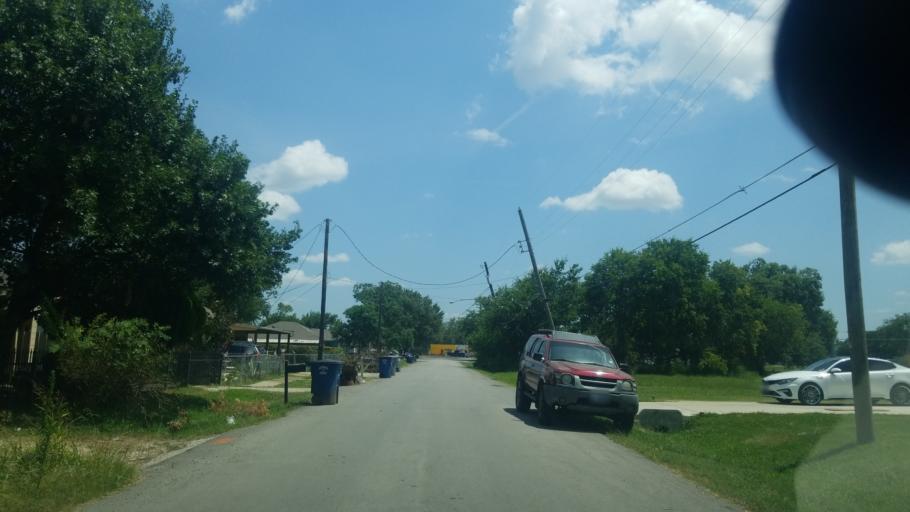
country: US
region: Texas
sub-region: Dallas County
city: Dallas
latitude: 32.7166
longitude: -96.7655
